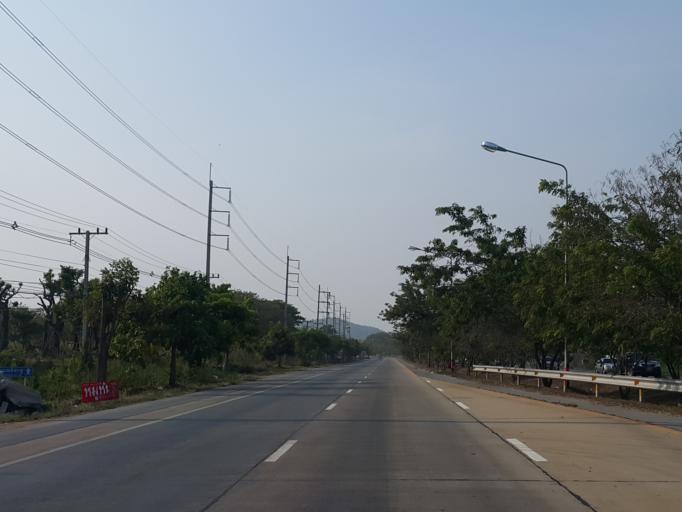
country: TH
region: Suphan Buri
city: Doembang Nangbuat
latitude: 14.8261
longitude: 100.1145
